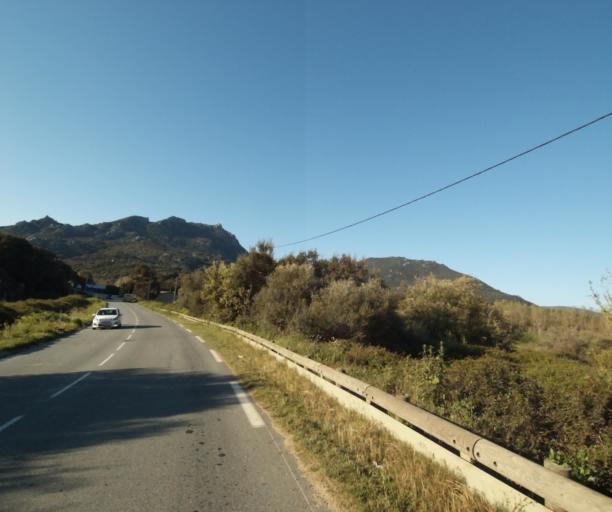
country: FR
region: Corsica
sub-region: Departement de la Corse-du-Sud
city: Propriano
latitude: 41.6605
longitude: 8.9169
